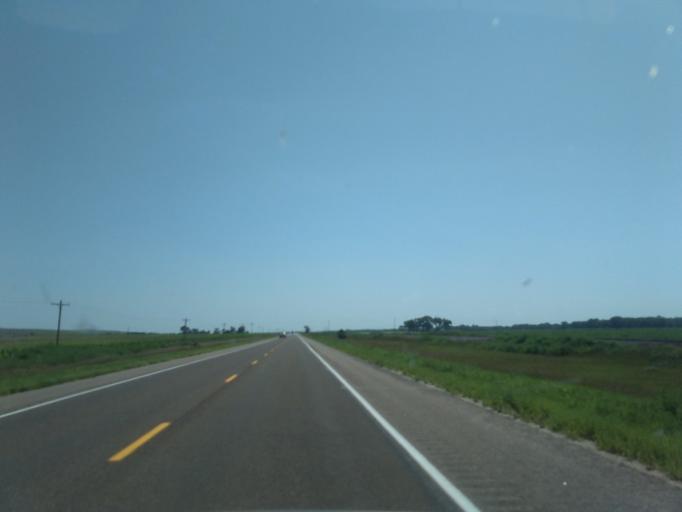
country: US
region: Nebraska
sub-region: Dundy County
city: Benkelman
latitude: 40.1265
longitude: -101.3116
